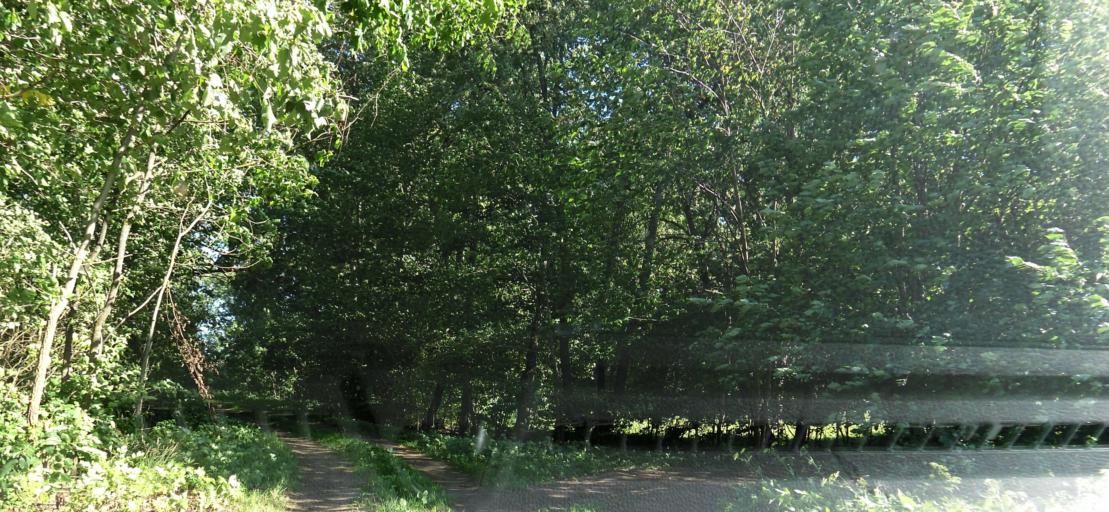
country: LT
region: Panevezys
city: Pasvalys
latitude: 56.1479
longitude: 24.4571
